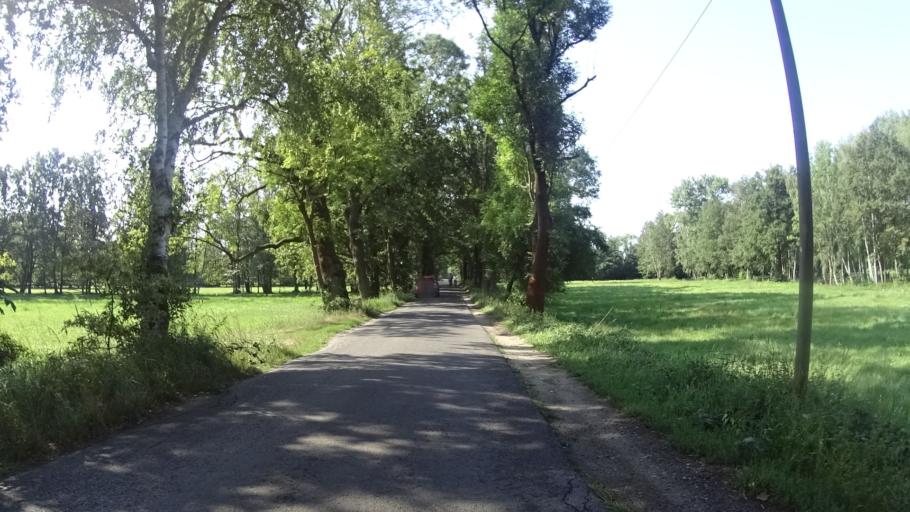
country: DE
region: Brandenburg
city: Straupitz
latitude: 51.8747
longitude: 14.1184
